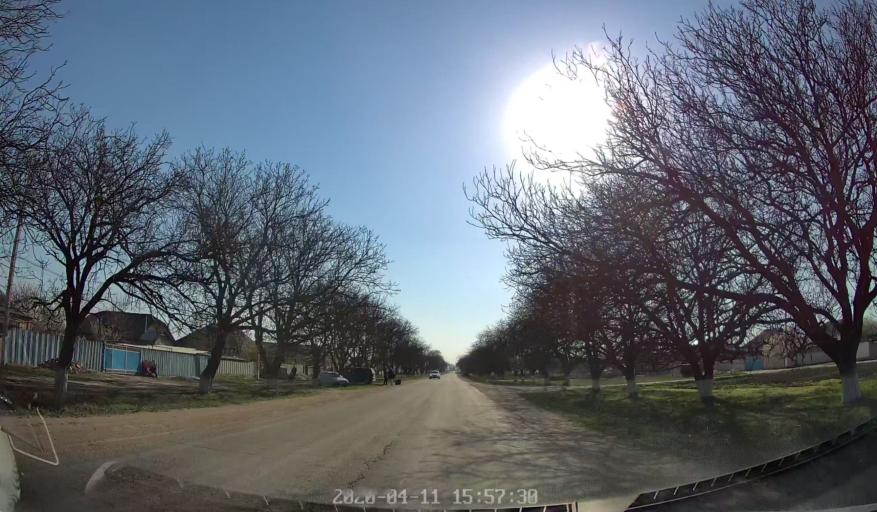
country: MD
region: Chisinau
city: Vadul lui Voda
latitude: 47.0889
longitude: 29.1679
